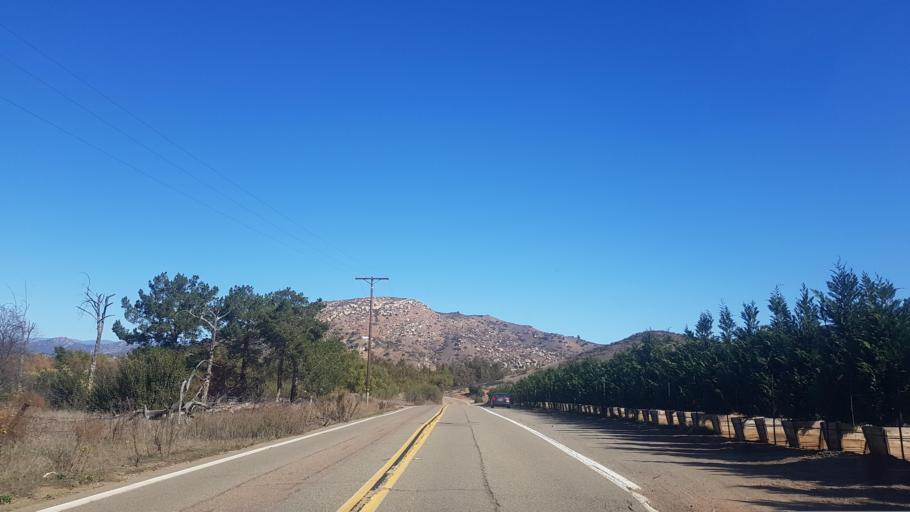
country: US
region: California
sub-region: San Diego County
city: Escondido
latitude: 33.0540
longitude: -117.0375
